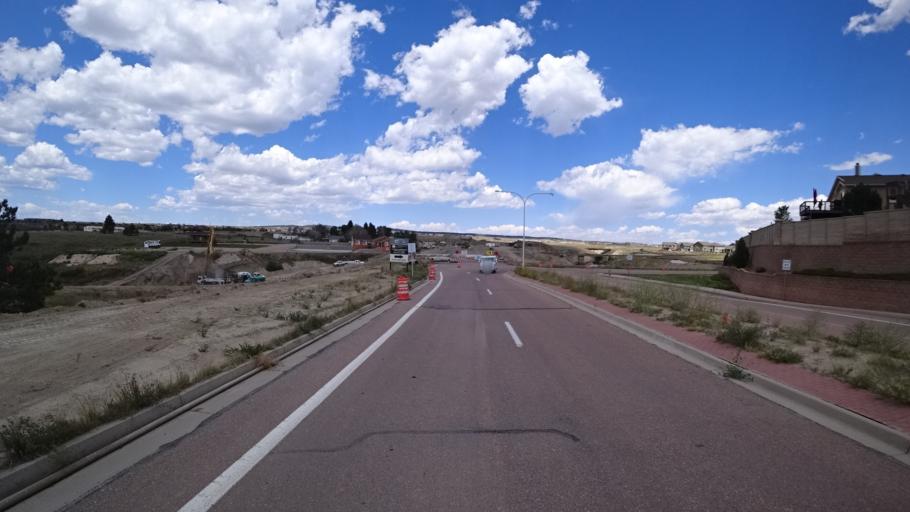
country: US
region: Colorado
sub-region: El Paso County
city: Black Forest
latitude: 38.9493
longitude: -104.7148
